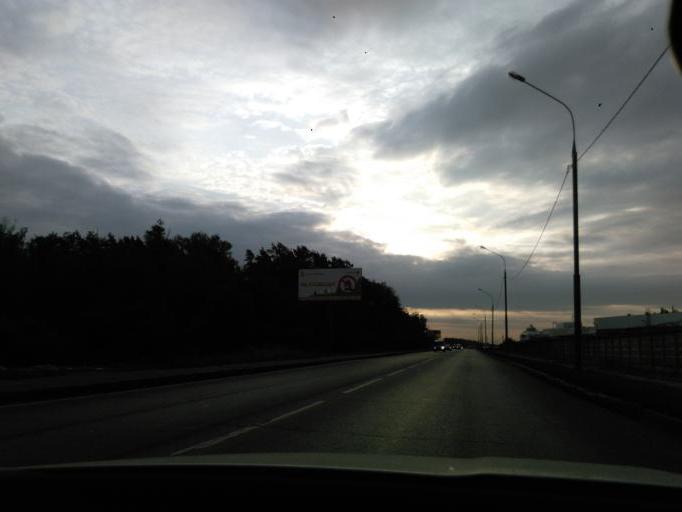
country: RU
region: Moskovskaya
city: Lobnya
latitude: 55.9845
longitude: 37.4328
